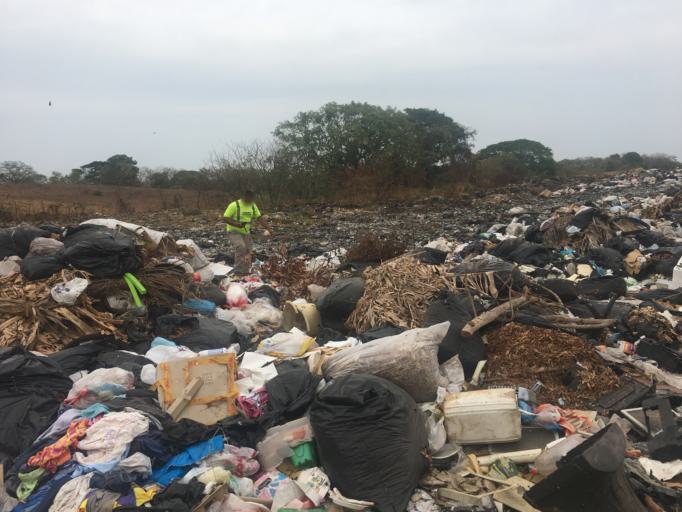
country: PA
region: Los Santos
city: Pedasi
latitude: 7.5480
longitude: -80.0827
